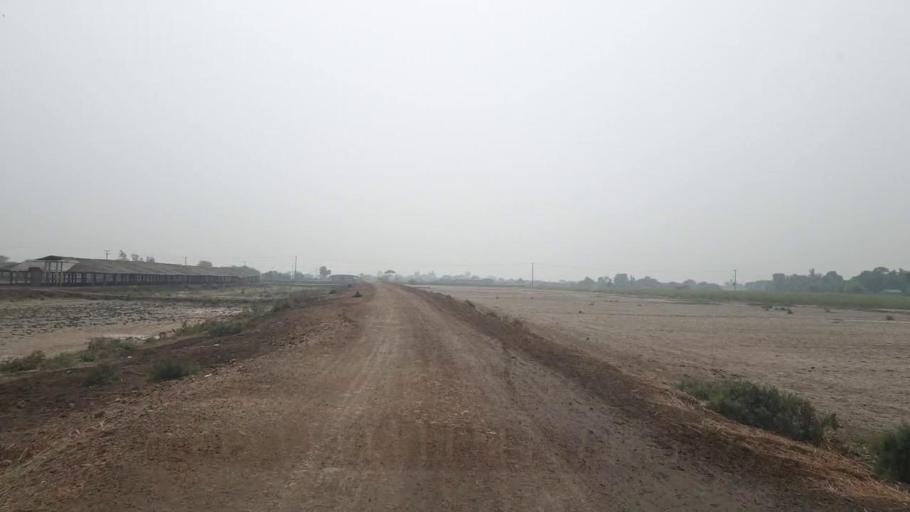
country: PK
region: Sindh
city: Kario
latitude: 24.6475
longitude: 68.6398
